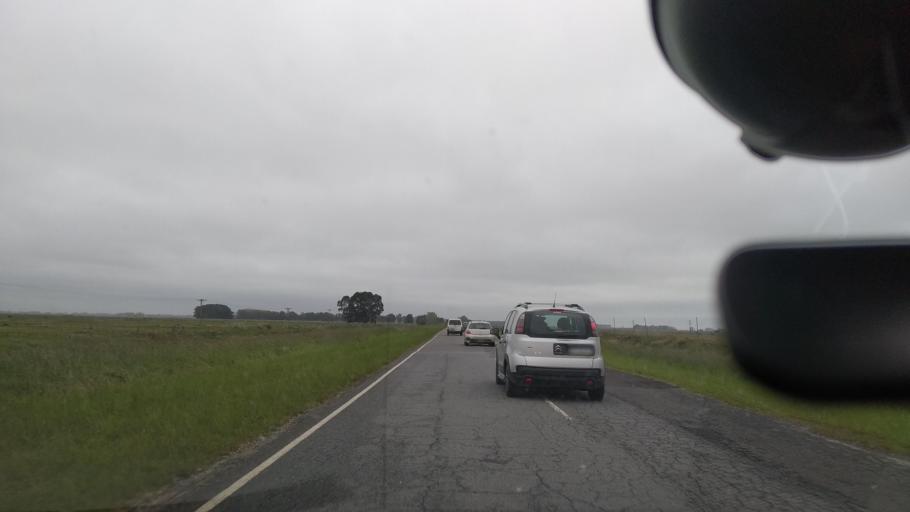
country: AR
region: Buenos Aires
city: Veronica
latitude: -35.5038
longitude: -57.3339
